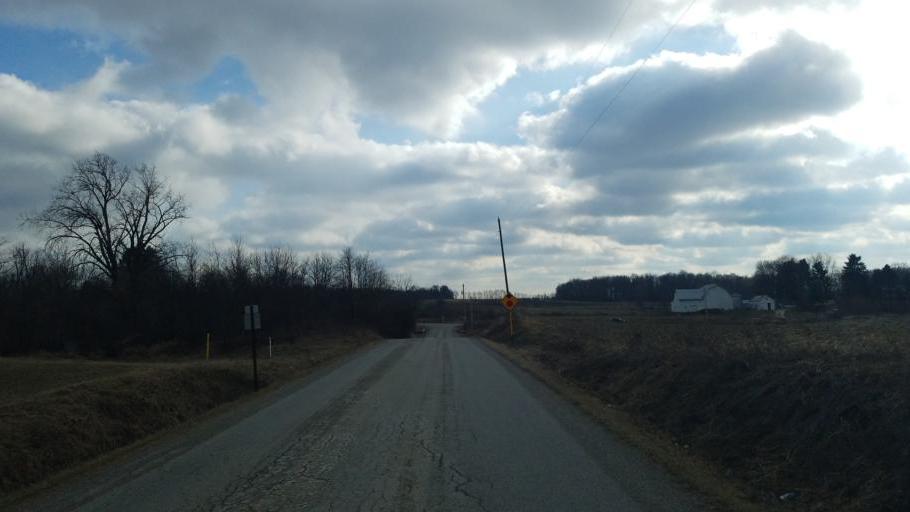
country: US
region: Ohio
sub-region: Morrow County
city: Mount Gilead
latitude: 40.5895
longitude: -82.7479
